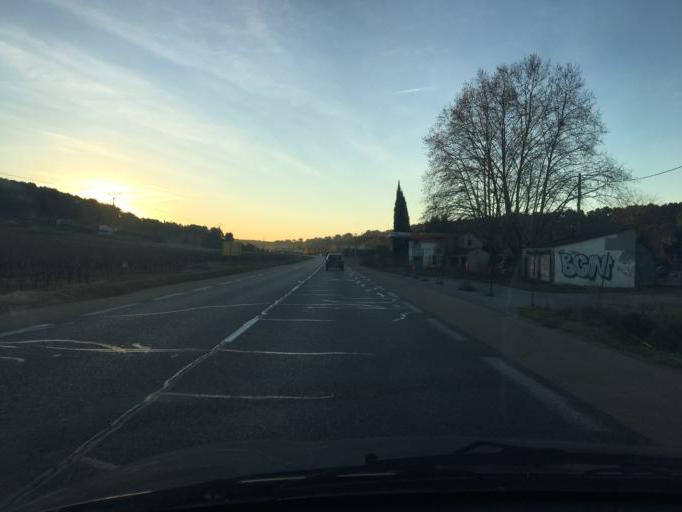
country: FR
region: Provence-Alpes-Cote d'Azur
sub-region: Departement du Var
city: Lorgues
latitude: 43.4772
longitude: 6.3737
